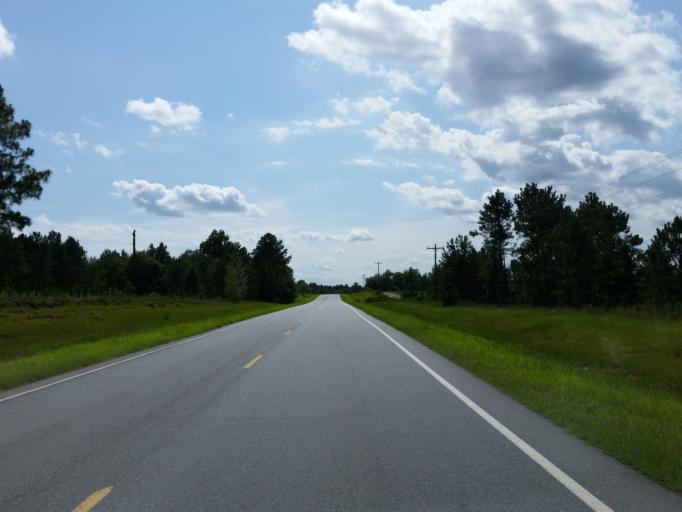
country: US
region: Georgia
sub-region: Turner County
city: Ashburn
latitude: 31.6352
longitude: -83.5026
